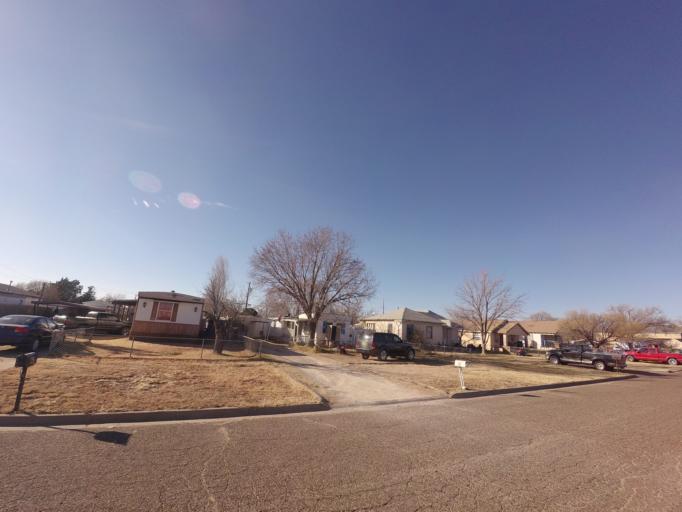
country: US
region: New Mexico
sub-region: Curry County
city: Clovis
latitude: 34.4033
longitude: -103.1801
